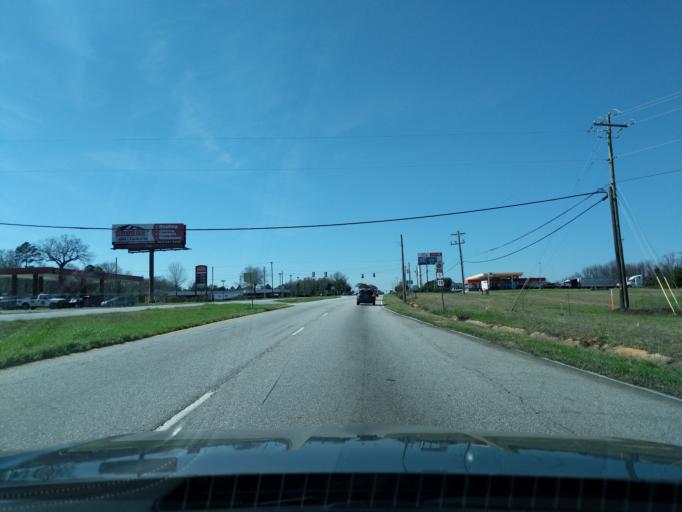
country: US
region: South Carolina
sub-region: Aiken County
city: Clearwater
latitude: 33.4881
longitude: -81.9241
